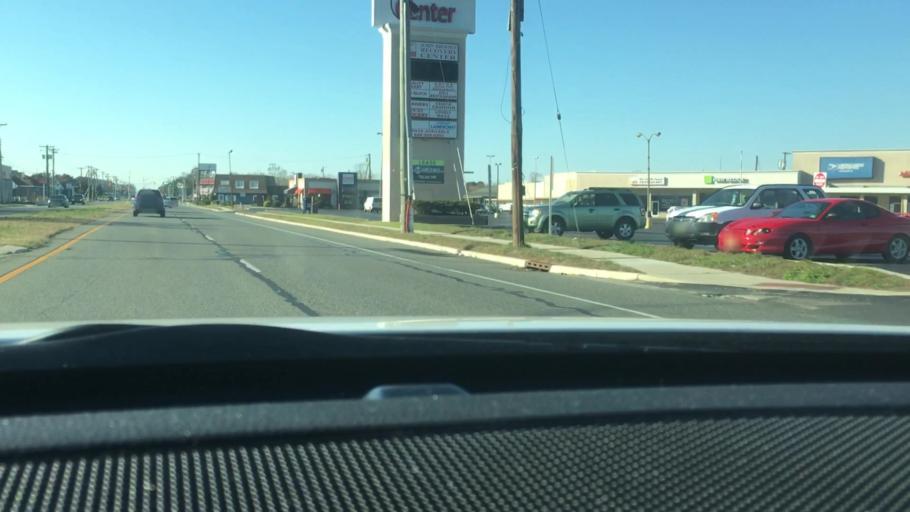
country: US
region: New Jersey
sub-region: Atlantic County
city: Pleasantville
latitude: 39.3934
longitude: -74.5376
